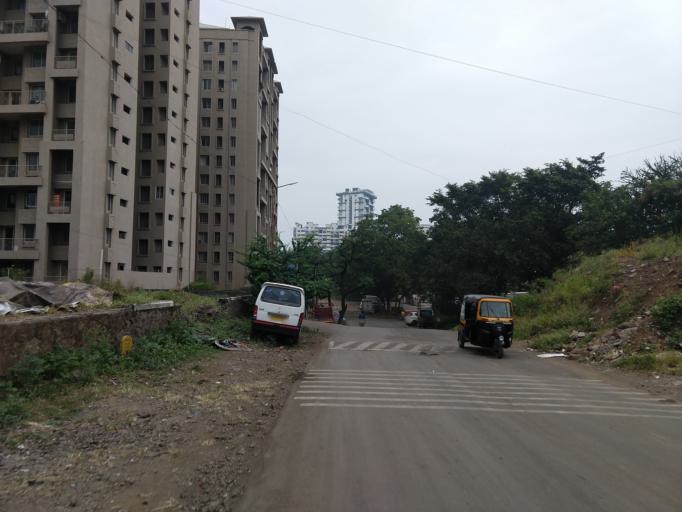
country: IN
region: Maharashtra
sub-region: Pune Division
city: Pune
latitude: 18.4550
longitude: 73.8842
